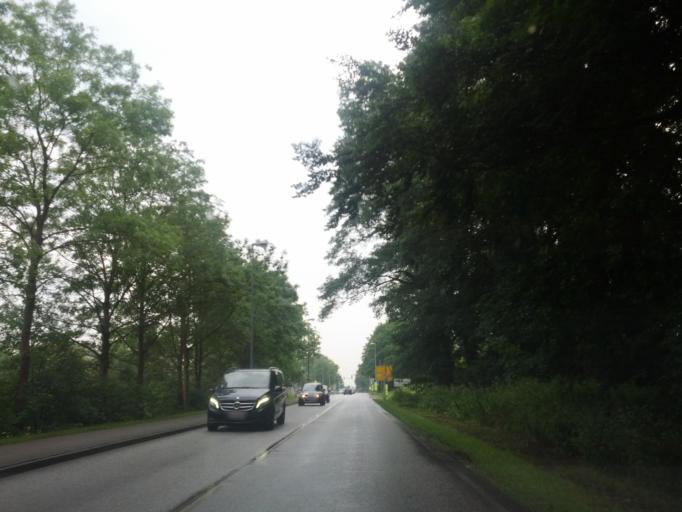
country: DE
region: Mecklenburg-Vorpommern
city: Bad Doberan
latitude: 54.1082
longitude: 11.9145
